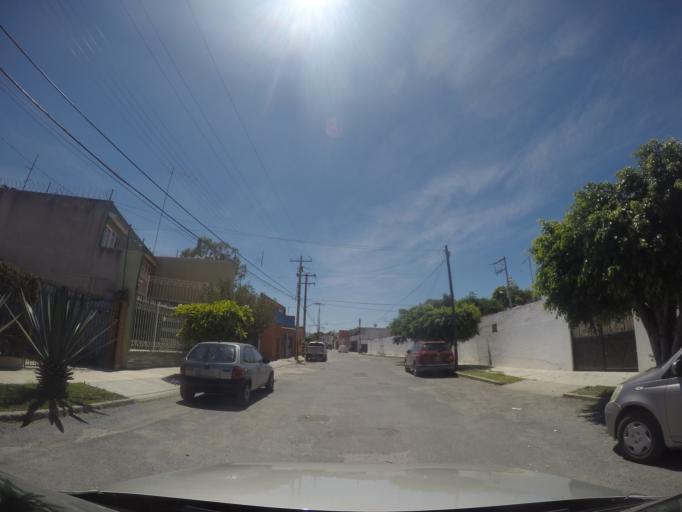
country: MX
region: San Luis Potosi
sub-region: San Luis Potosi
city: San Luis Potosi
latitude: 22.1581
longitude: -100.9883
